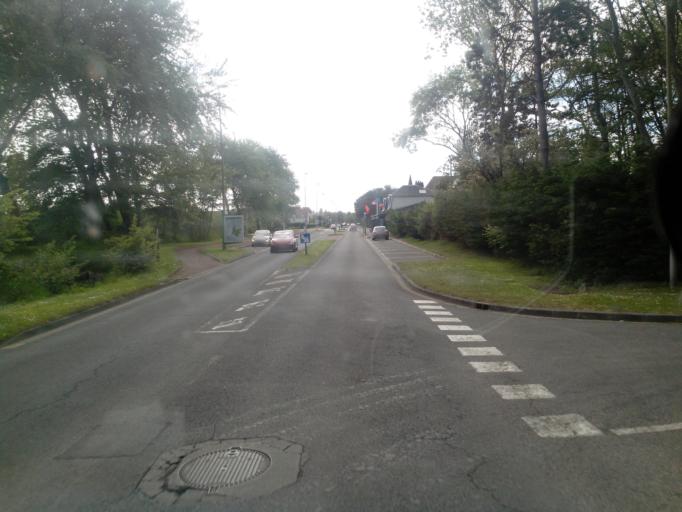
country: FR
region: Lower Normandy
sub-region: Departement du Calvados
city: Cabourg
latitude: 49.2844
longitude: -0.1522
